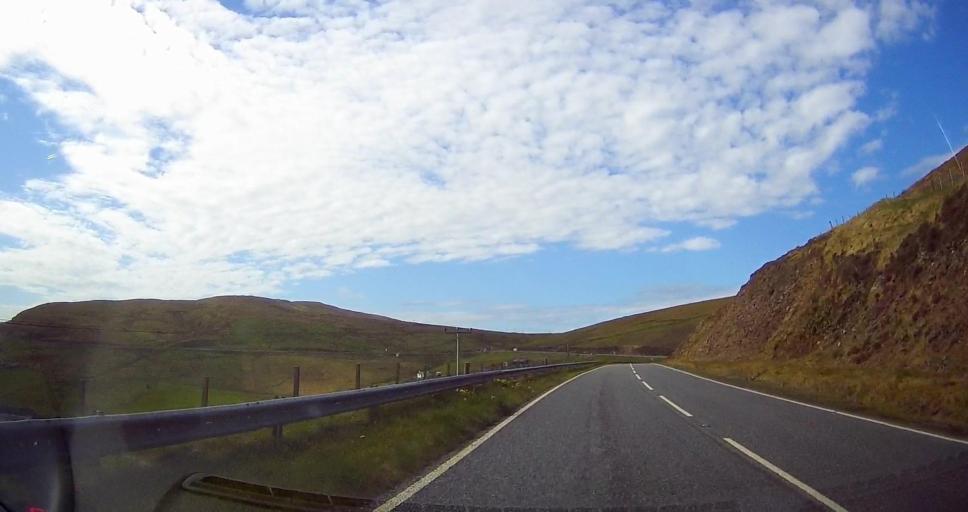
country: GB
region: Scotland
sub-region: Shetland Islands
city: Sandwick
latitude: 59.9930
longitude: -1.2791
